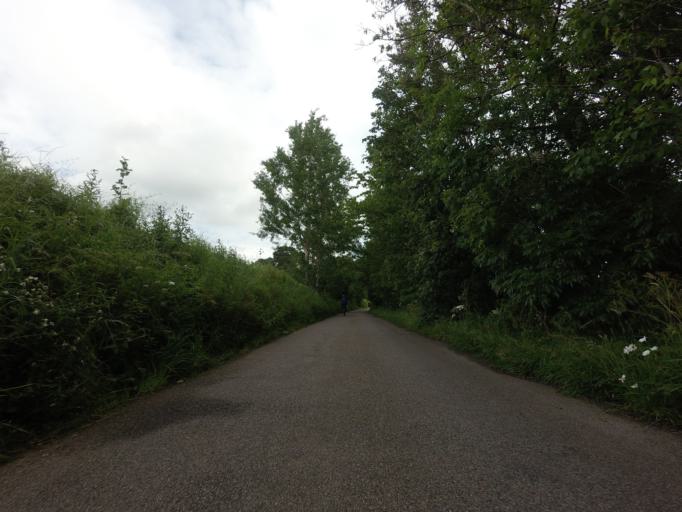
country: GB
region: Scotland
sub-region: Moray
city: Lhanbryd
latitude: 57.6525
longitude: -3.2364
